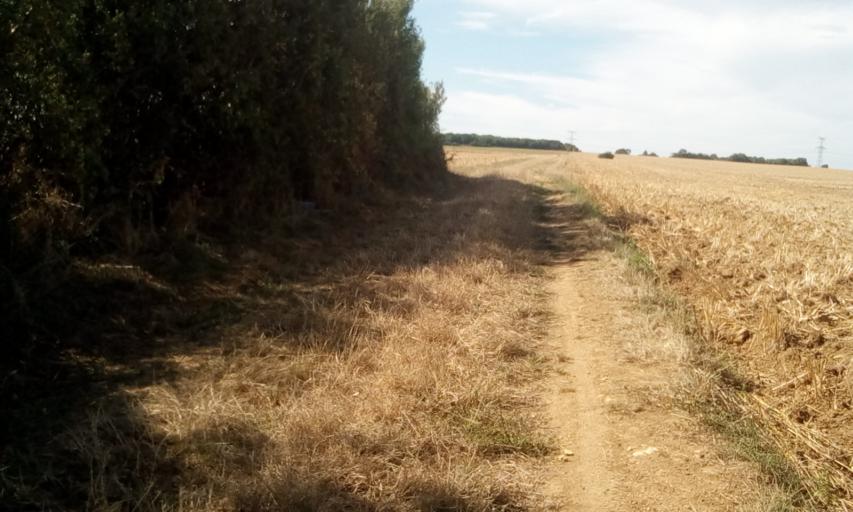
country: FR
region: Lower Normandy
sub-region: Departement du Calvados
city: Fontaine-Etoupefour
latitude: 49.1111
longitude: -0.4474
